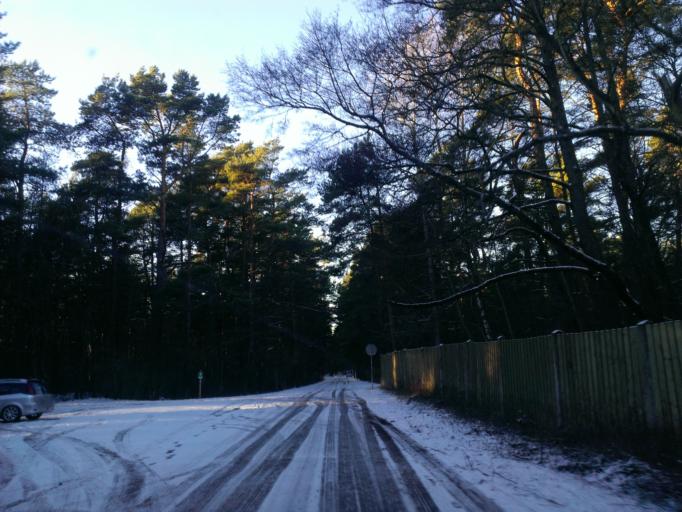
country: LV
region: Riga
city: Bolderaja
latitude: 57.0709
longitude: 24.0884
